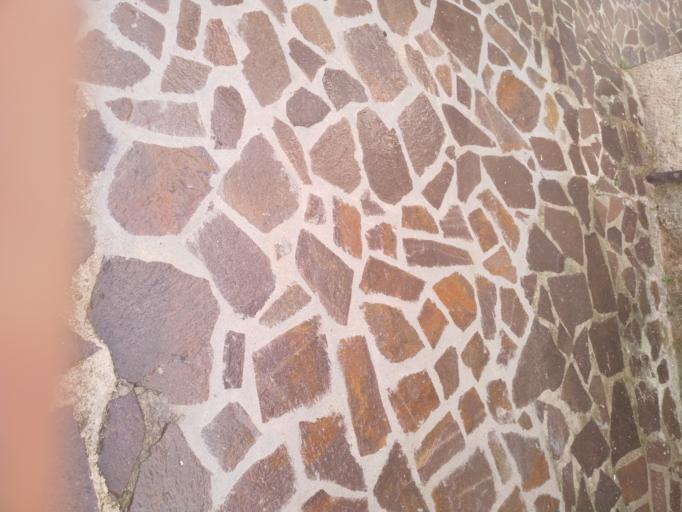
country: IT
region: Abruzzo
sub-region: Provincia di Teramo
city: Castelli
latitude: 42.4880
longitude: 13.7116
